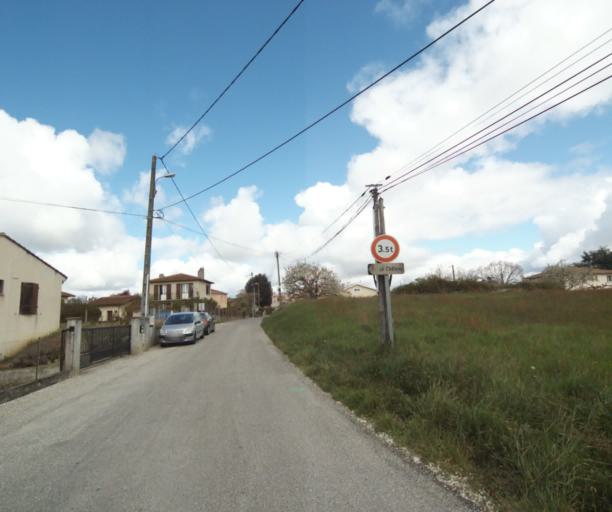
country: FR
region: Midi-Pyrenees
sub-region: Departement de l'Ariege
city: Saverdun
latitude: 43.2271
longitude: 1.5773
